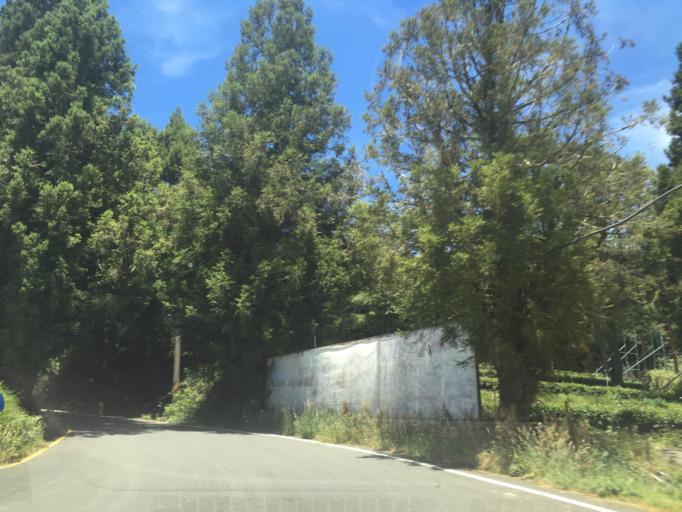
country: TW
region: Taiwan
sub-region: Nantou
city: Puli
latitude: 24.2304
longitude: 121.2435
